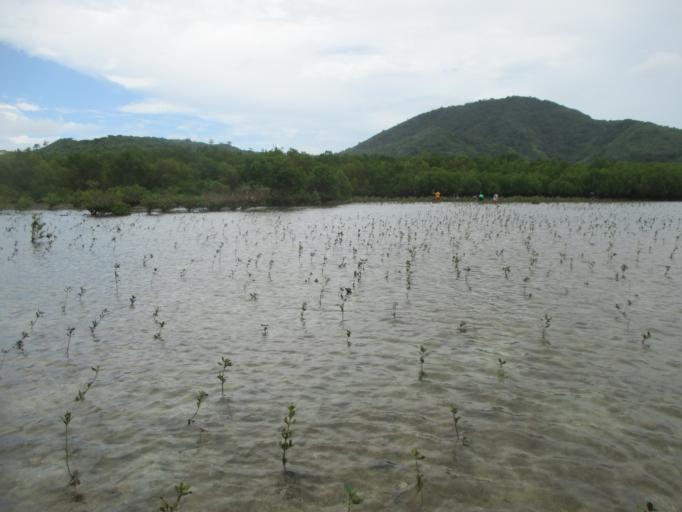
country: PH
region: Calabarzon
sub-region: Province of Batangas
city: Binubusan
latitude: 13.9952
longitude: 120.6224
